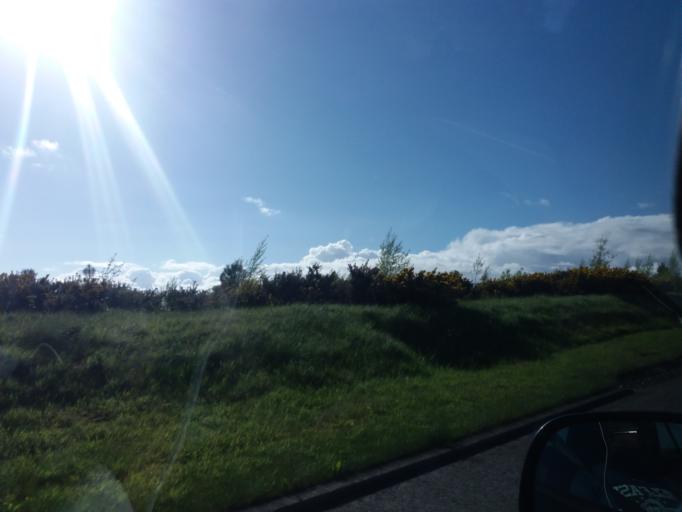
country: IE
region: Munster
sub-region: Waterford
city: Waterford
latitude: 52.3379
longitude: -7.1615
